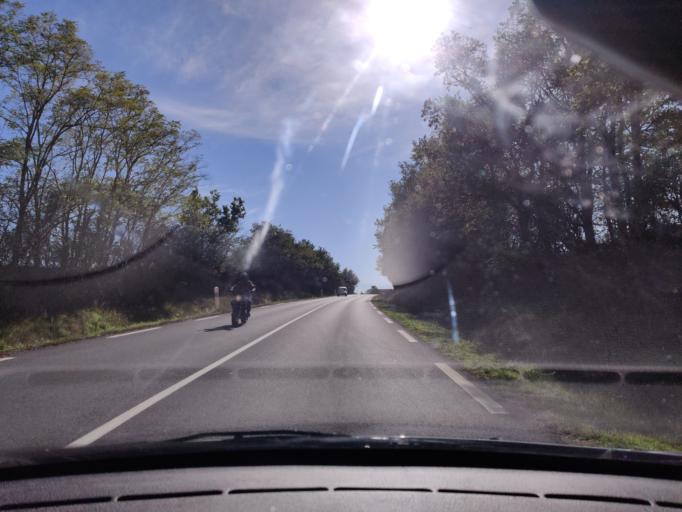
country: FR
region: Auvergne
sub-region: Departement du Puy-de-Dome
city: Combronde
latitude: 46.0043
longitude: 3.0938
